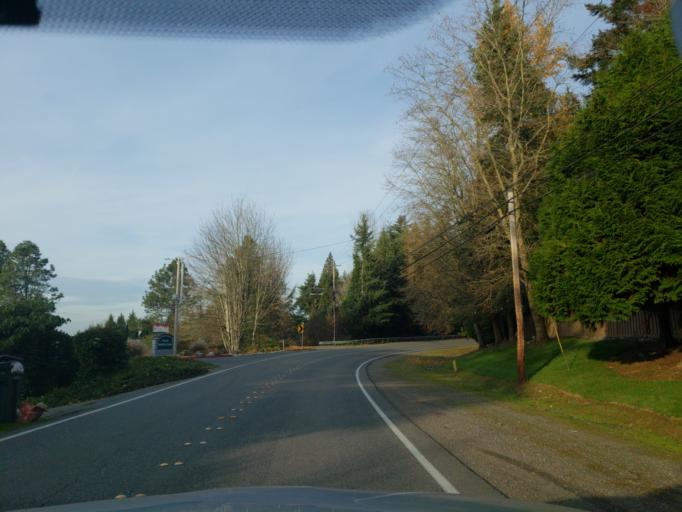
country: US
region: Washington
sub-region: Snohomish County
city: Maltby
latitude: 47.7927
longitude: -122.1330
